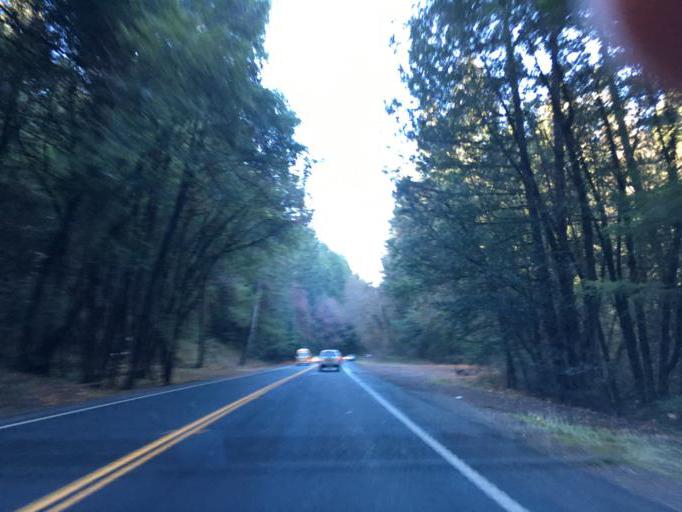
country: US
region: California
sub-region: Mendocino County
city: Brooktrails
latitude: 39.5012
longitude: -123.3769
